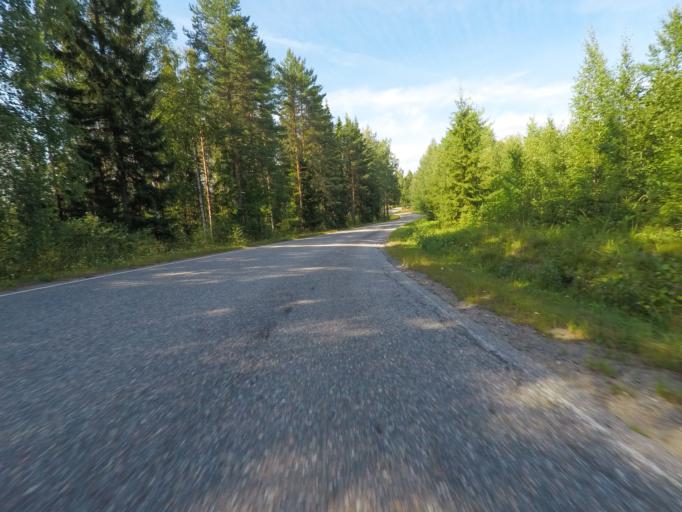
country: FI
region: Southern Savonia
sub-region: Mikkeli
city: Puumala
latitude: 61.5868
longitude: 28.1862
